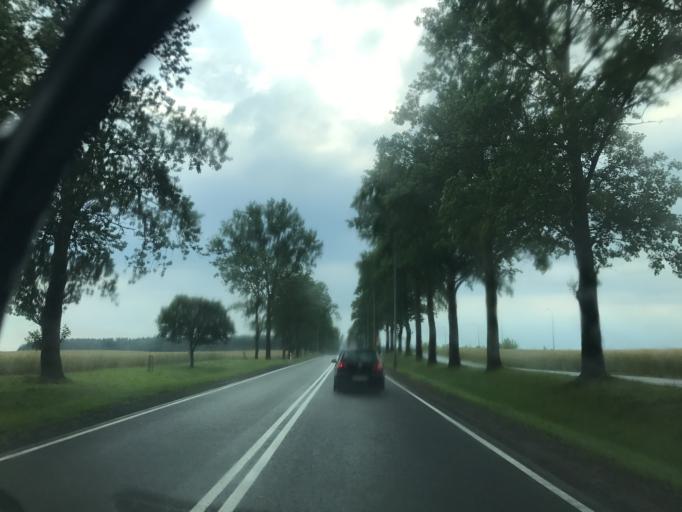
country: PL
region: Pomeranian Voivodeship
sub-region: Powiat czluchowski
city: Czluchow
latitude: 53.6873
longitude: 17.4529
